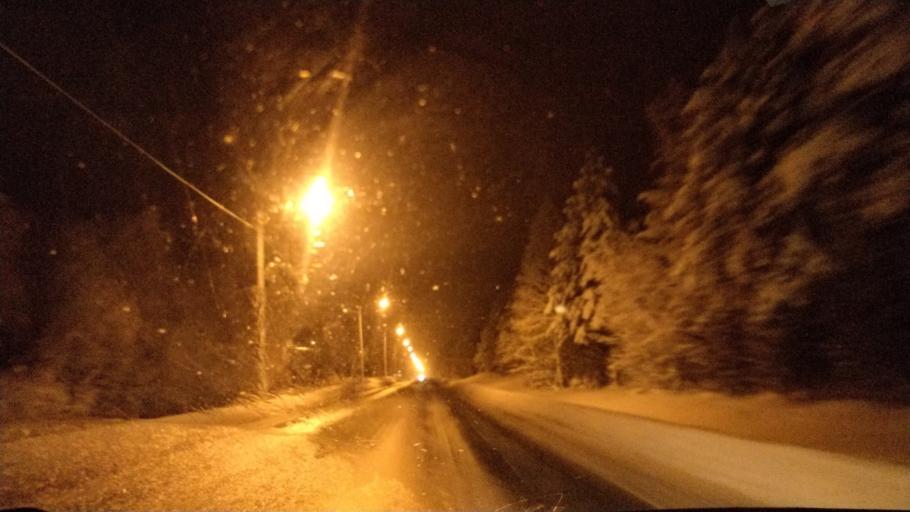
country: FI
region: Lapland
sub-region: Rovaniemi
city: Rovaniemi
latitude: 66.4570
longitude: 25.5862
